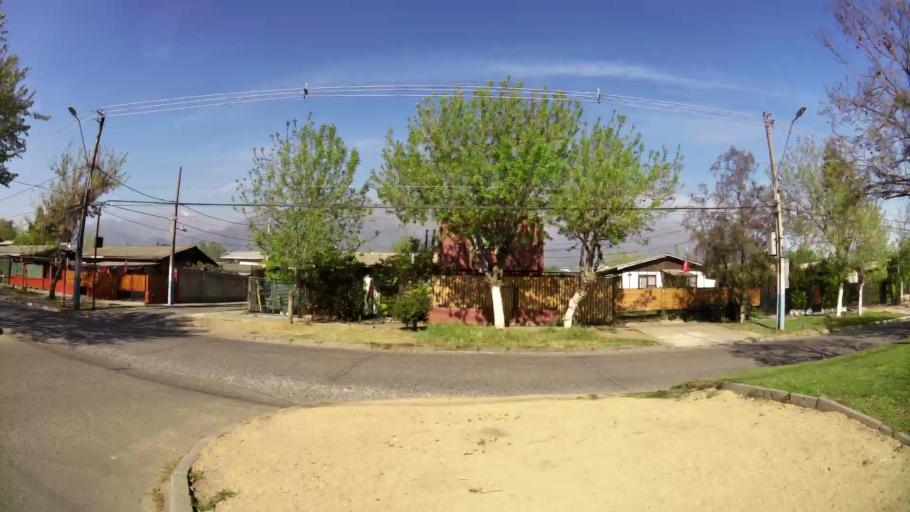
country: CL
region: Santiago Metropolitan
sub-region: Provincia de Santiago
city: Villa Presidente Frei, Nunoa, Santiago, Chile
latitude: -33.4635
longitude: -70.5660
